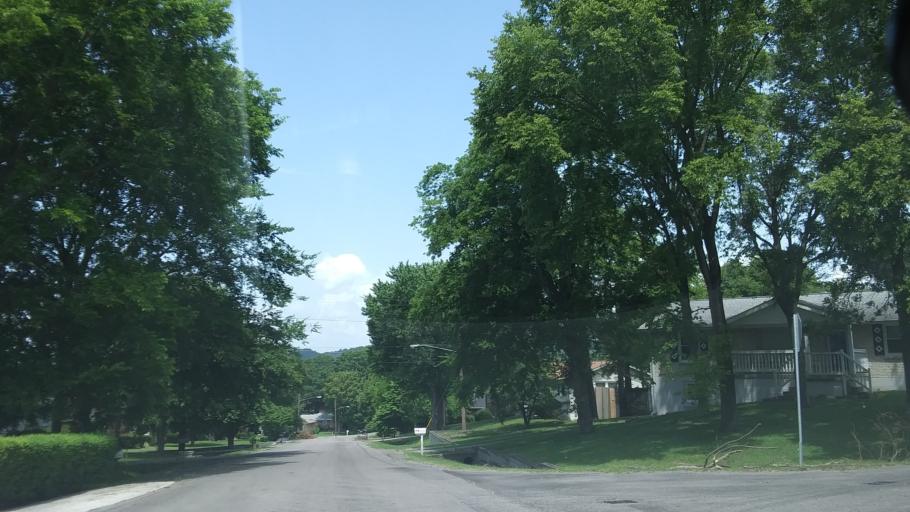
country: US
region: Tennessee
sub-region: Davidson County
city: Belle Meade
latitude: 36.1461
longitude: -86.8851
